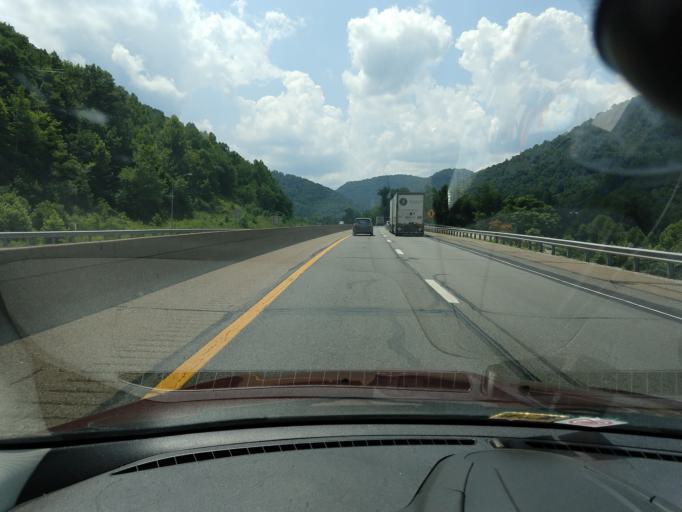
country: US
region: West Virginia
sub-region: Kanawha County
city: Chesapeake
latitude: 38.1563
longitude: -81.4470
